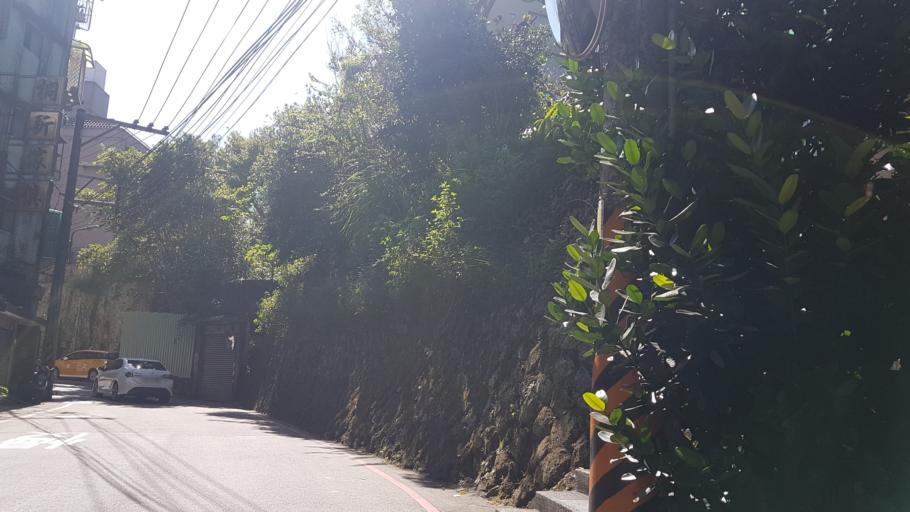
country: TW
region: Taipei
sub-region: Taipei
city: Banqiao
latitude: 24.9548
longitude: 121.5319
